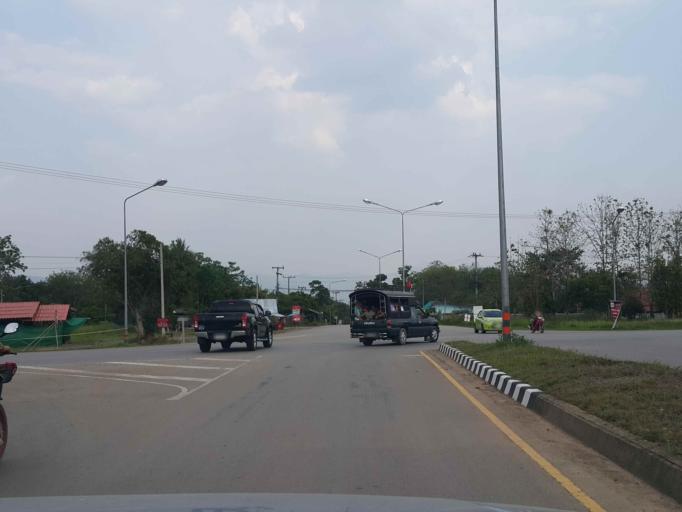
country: TH
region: Chiang Mai
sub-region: Amphoe Chiang Dao
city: Chiang Dao
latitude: 19.3774
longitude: 98.9459
